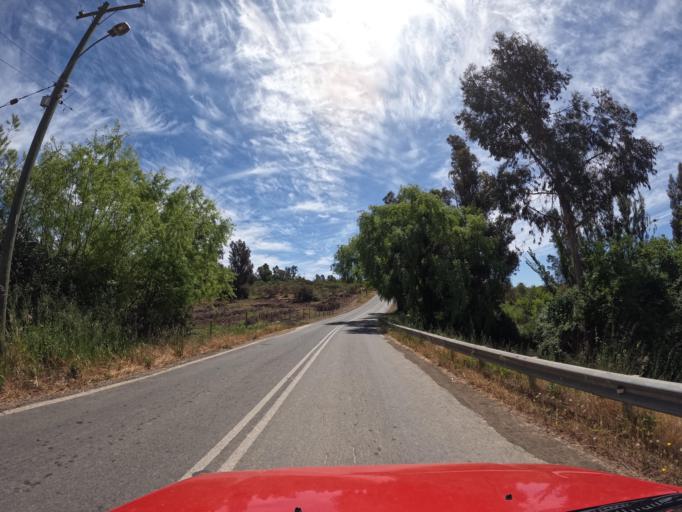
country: CL
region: Maule
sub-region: Provincia de Talca
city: Talca
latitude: -35.0080
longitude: -71.7868
